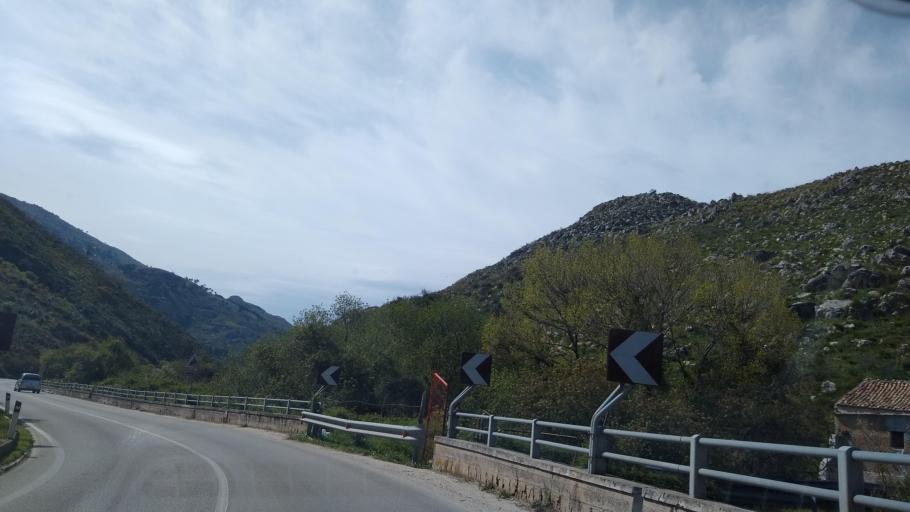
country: IT
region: Sicily
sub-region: Palermo
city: Pioppo
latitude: 38.0486
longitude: 13.1976
